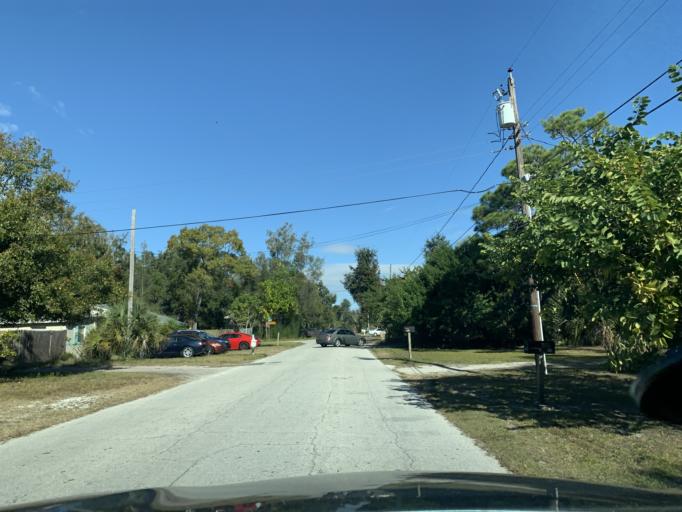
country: US
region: Florida
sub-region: Pinellas County
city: Bay Pines
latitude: 27.8148
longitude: -82.7497
